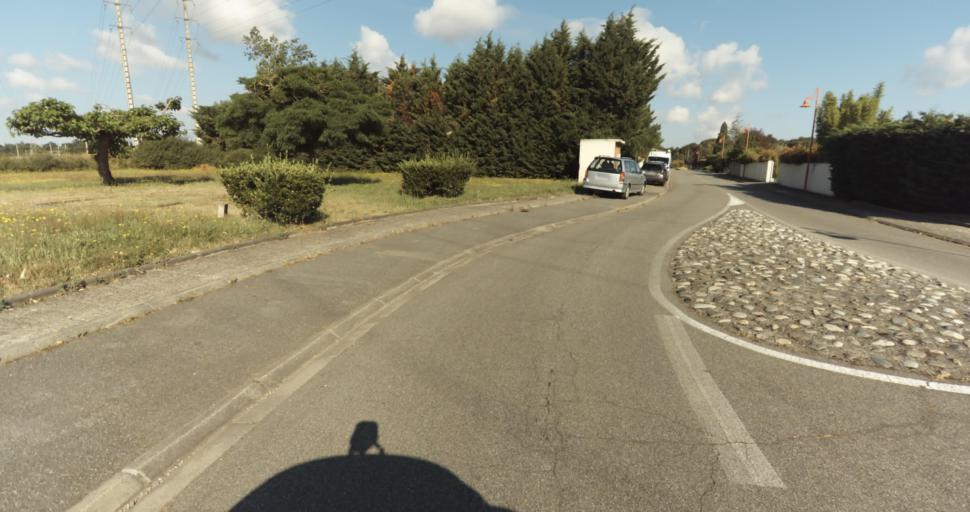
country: FR
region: Midi-Pyrenees
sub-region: Departement de la Haute-Garonne
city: Fontenilles
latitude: 43.5668
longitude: 1.2029
